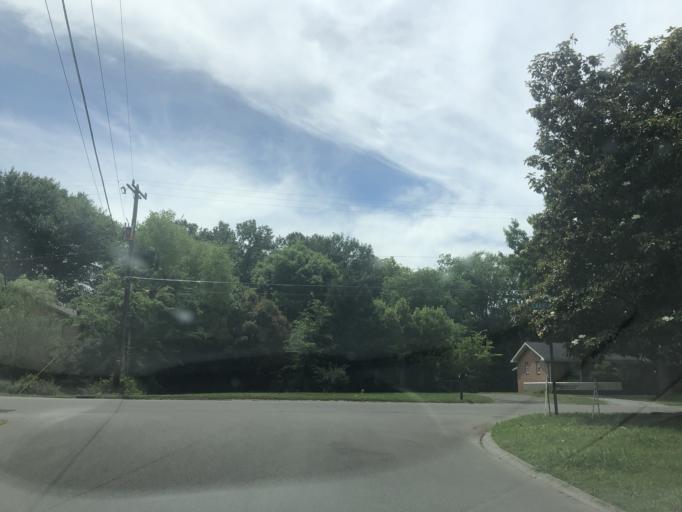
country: US
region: Tennessee
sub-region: Davidson County
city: Belle Meade
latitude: 36.0783
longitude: -86.9422
